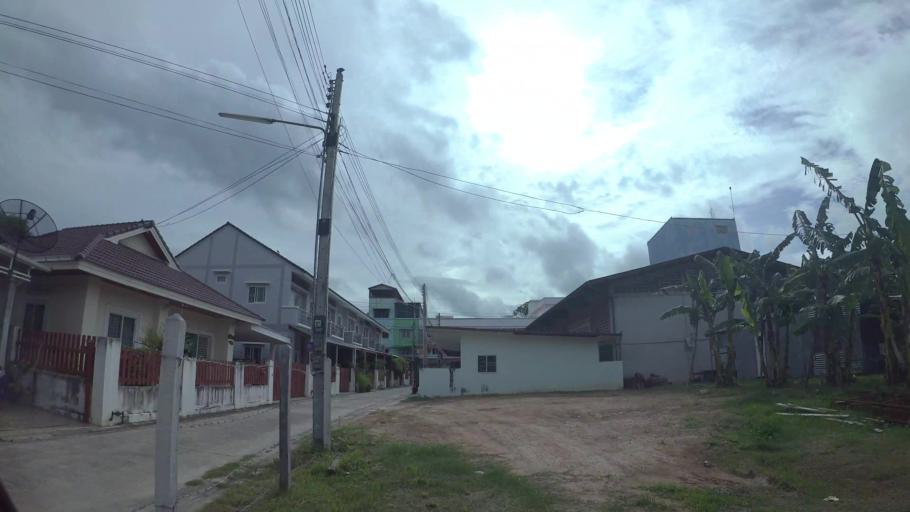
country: TH
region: Rayong
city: Rayong
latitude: 12.6726
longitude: 101.2798
